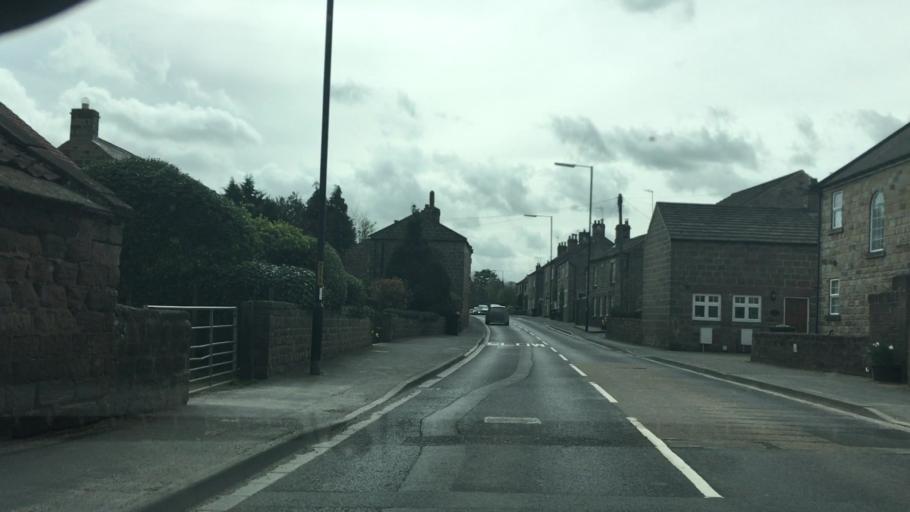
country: GB
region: England
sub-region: City and Borough of Leeds
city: Collingham
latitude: 53.9528
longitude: -1.4466
